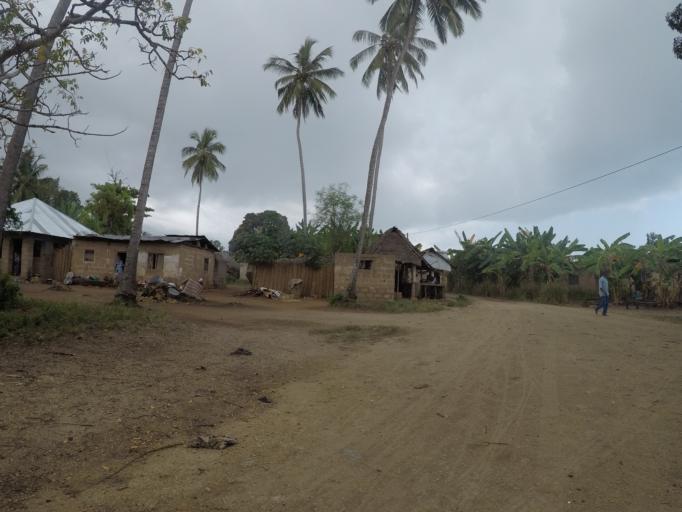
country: TZ
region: Zanzibar North
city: Mkokotoni
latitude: -5.9494
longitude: 39.1957
